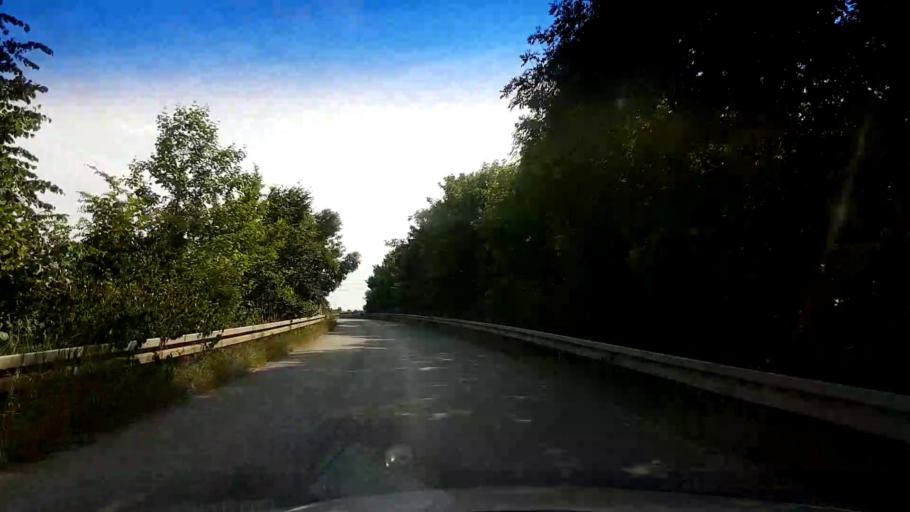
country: DE
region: Bavaria
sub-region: Regierungsbezirk Unterfranken
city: Stettfeld
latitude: 49.9676
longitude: 10.7216
